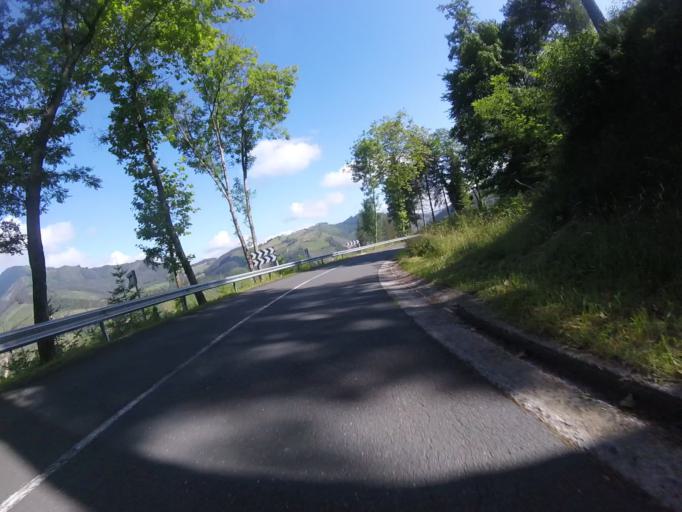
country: ES
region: Basque Country
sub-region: Provincia de Guipuzcoa
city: Ormaiztegui
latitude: 43.0935
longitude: -2.2418
